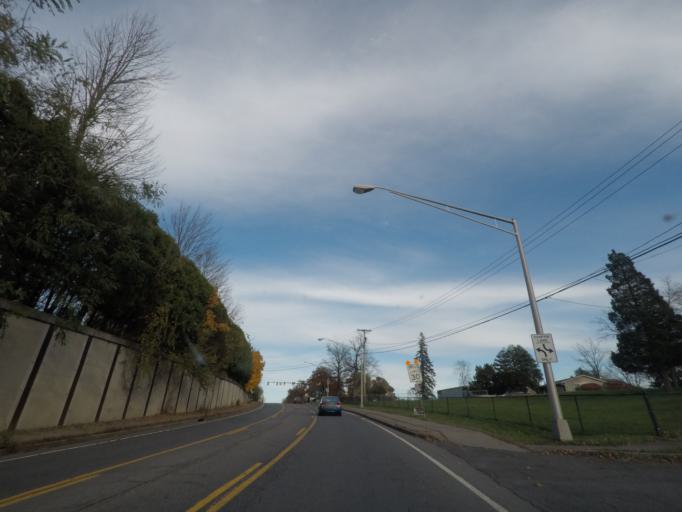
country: US
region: New York
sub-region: Albany County
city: Delmar
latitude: 42.6344
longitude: -73.7956
